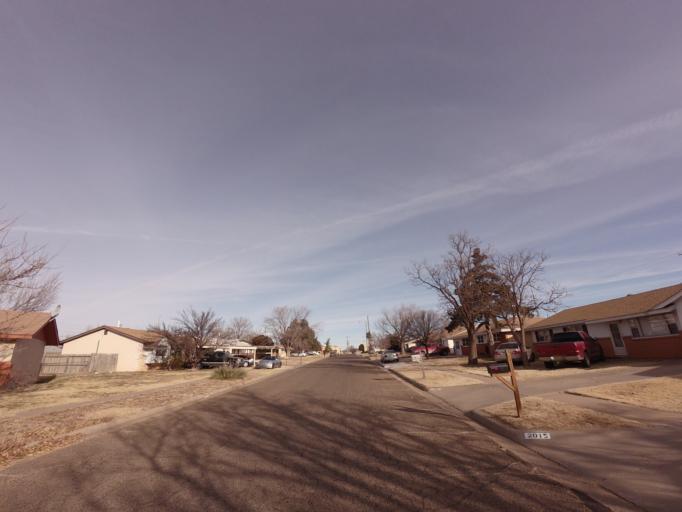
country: US
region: New Mexico
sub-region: Curry County
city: Clovis
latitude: 34.4179
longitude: -103.2191
